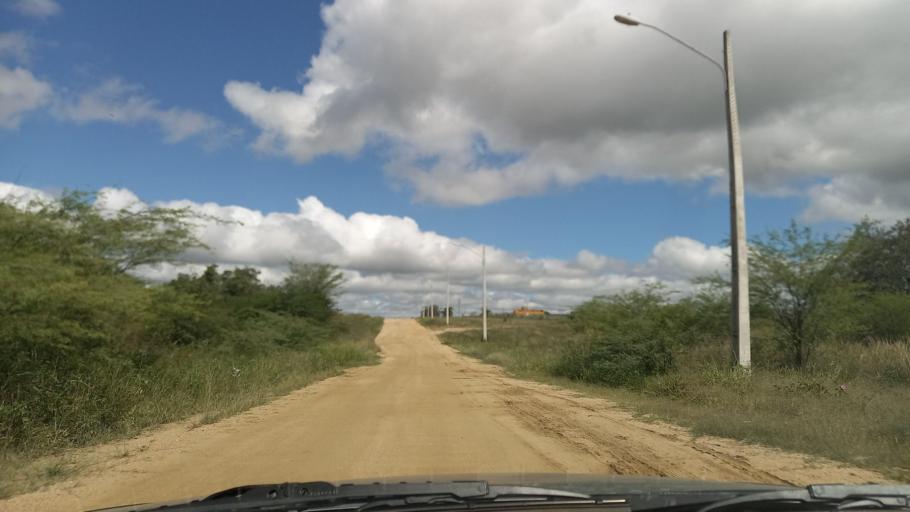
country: BR
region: Pernambuco
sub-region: Caruaru
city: Caruaru
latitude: -8.2318
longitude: -35.9798
